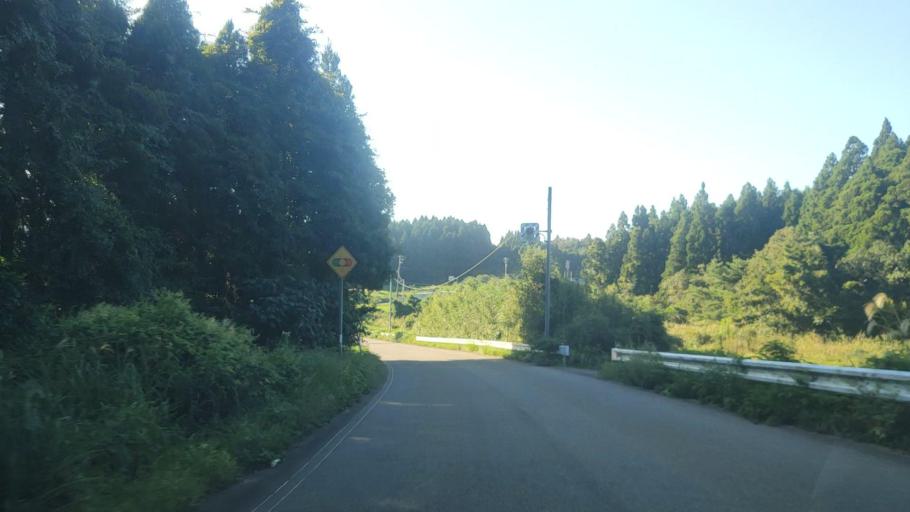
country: JP
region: Ishikawa
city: Nanao
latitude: 37.1241
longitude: 136.9339
